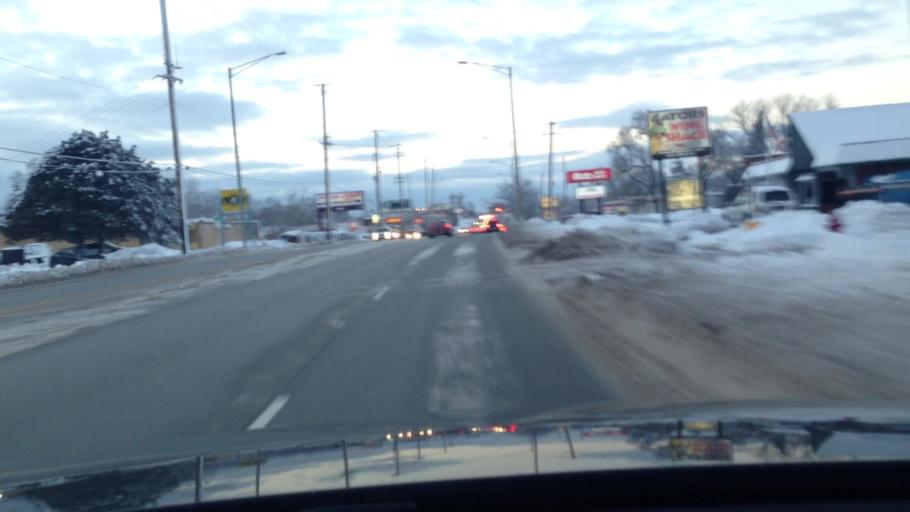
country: US
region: Illinois
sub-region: Cook County
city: Palatine
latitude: 42.1403
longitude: -88.0232
